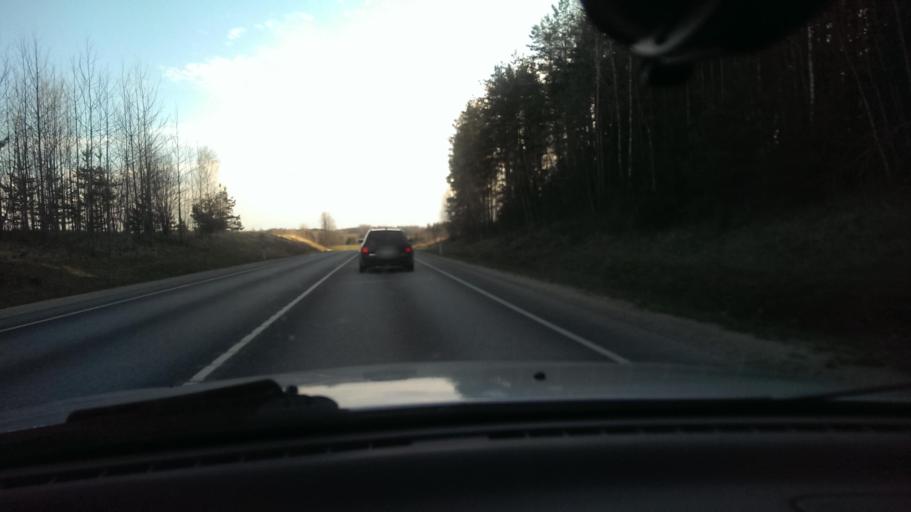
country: EE
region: Tartu
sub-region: UElenurme vald
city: Ulenurme
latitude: 58.1993
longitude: 26.7046
